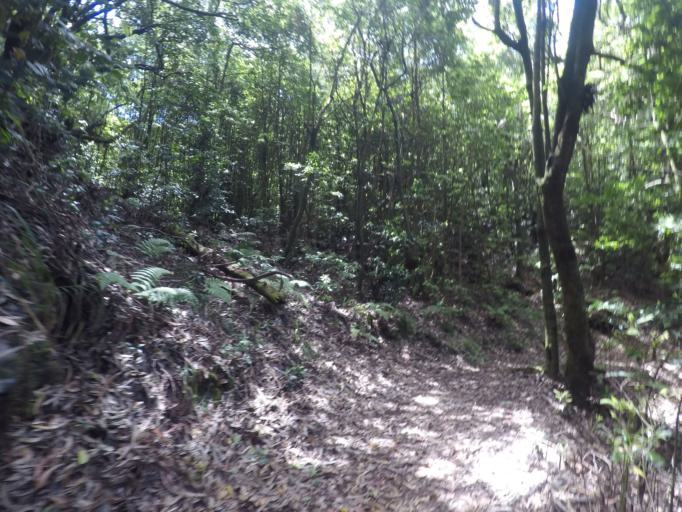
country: PT
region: Madeira
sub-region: Porto Moniz
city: Porto Moniz
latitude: 32.8367
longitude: -17.1434
